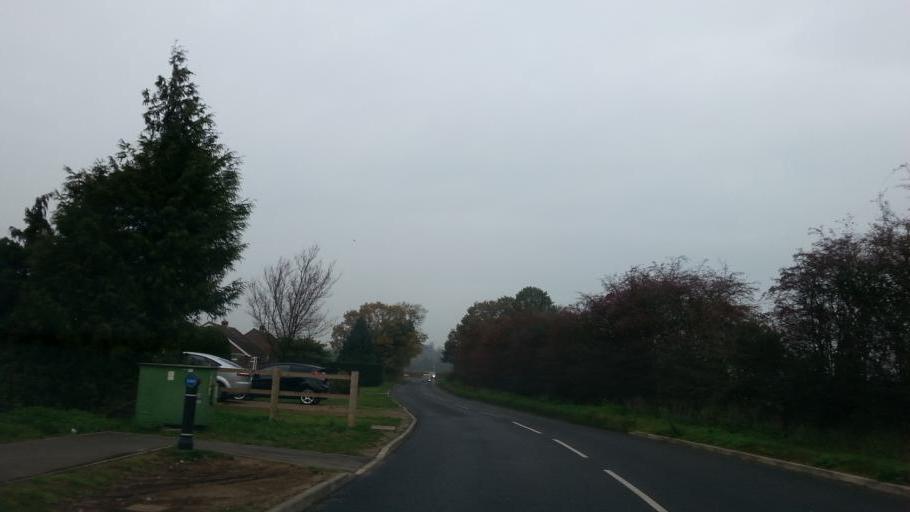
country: GB
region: England
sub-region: Suffolk
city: Thurston
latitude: 52.2460
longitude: 0.7802
